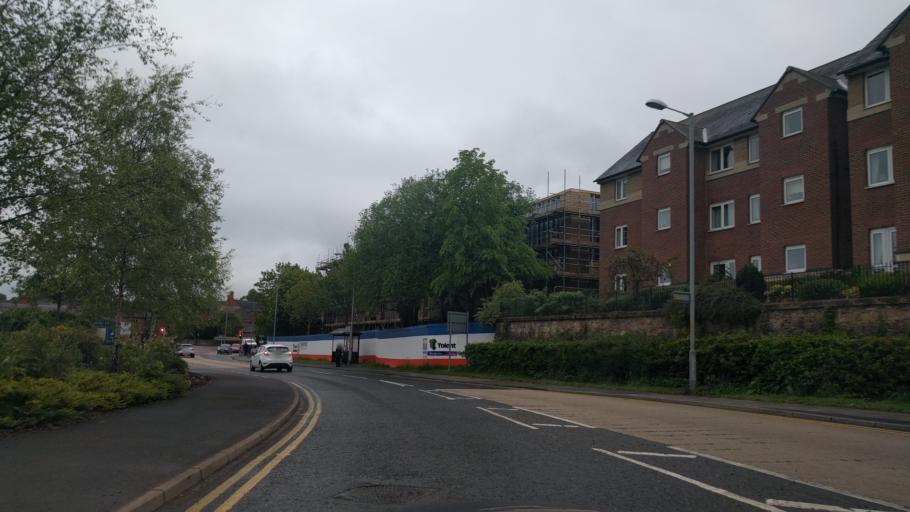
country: GB
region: England
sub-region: Northumberland
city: Morpeth
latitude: 55.1695
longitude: -1.6860
